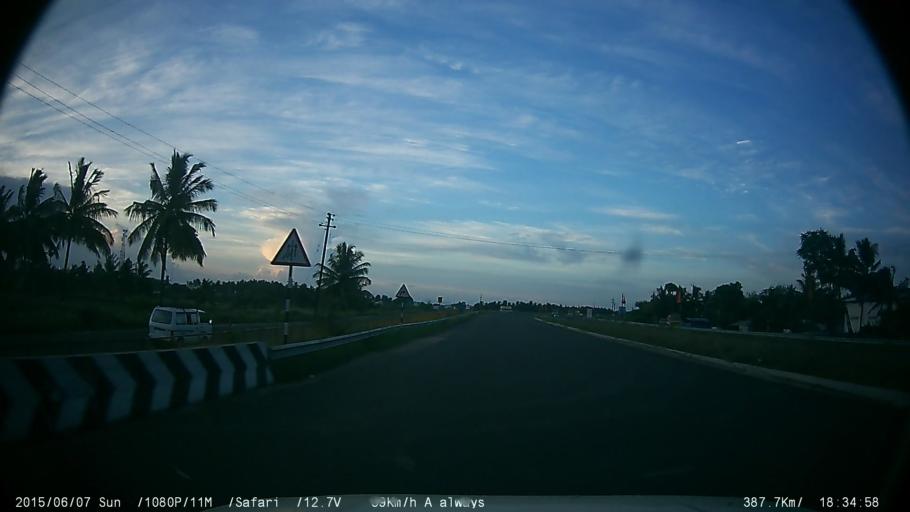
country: IN
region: Tamil Nadu
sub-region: Tiruppur
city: Avinashi
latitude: 11.1851
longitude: 77.2856
